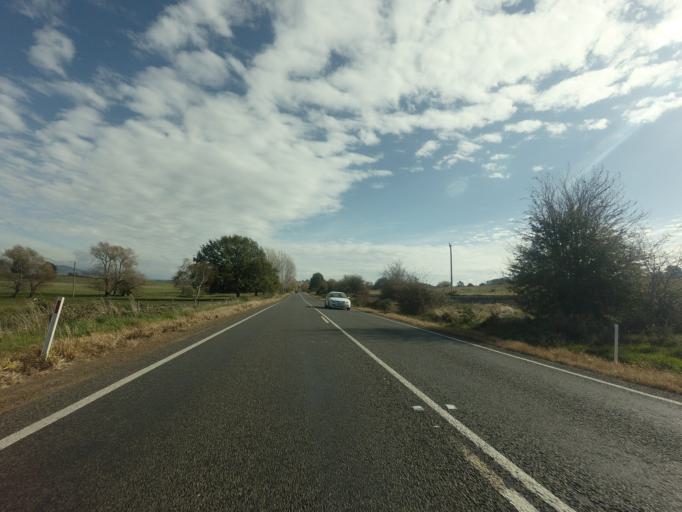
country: AU
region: Tasmania
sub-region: Meander Valley
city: Westbury
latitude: -41.5277
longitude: 146.8097
